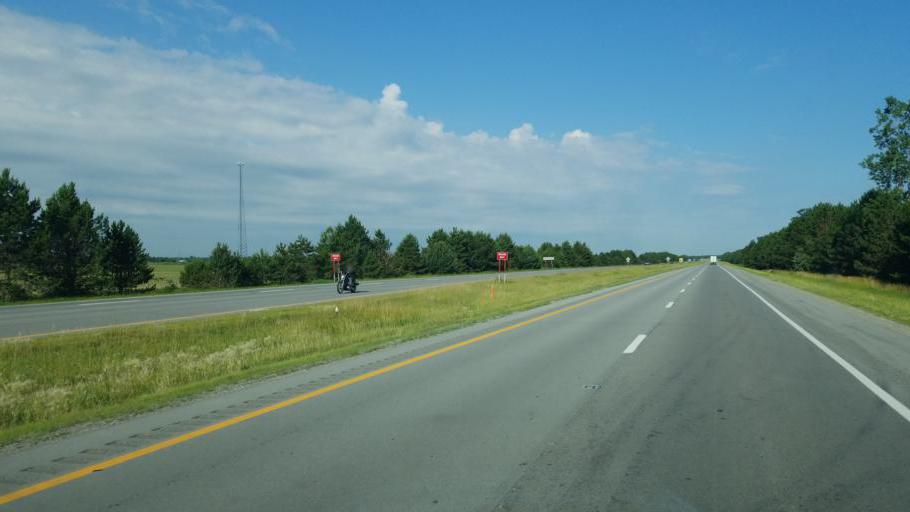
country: US
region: Ohio
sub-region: Hancock County
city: Findlay
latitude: 40.9863
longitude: -83.6129
